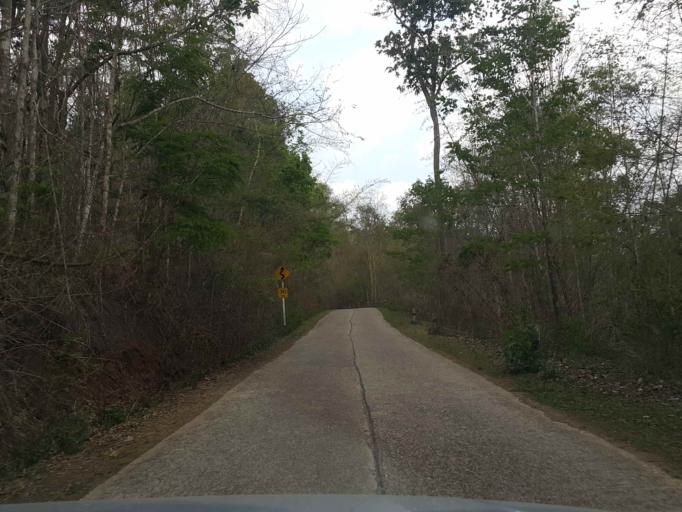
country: TH
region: Chiang Mai
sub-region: Amphoe Chiang Dao
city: Chiang Dao
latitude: 19.3809
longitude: 98.7700
